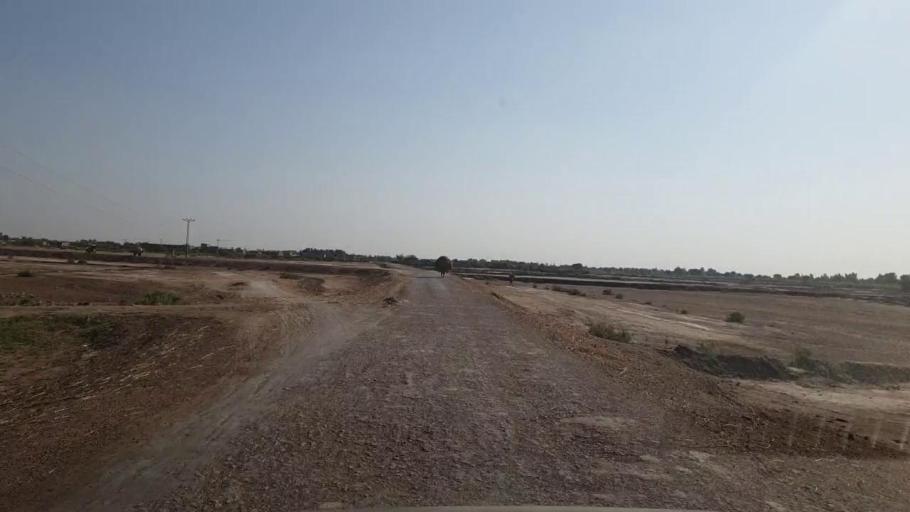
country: PK
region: Sindh
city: Matli
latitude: 25.0433
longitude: 68.7231
